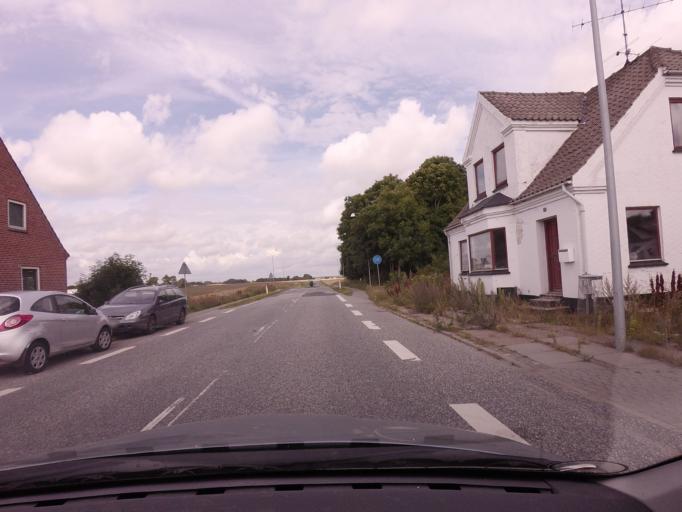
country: DK
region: North Denmark
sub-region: Hjorring Kommune
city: Sindal
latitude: 57.3383
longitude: 10.3035
